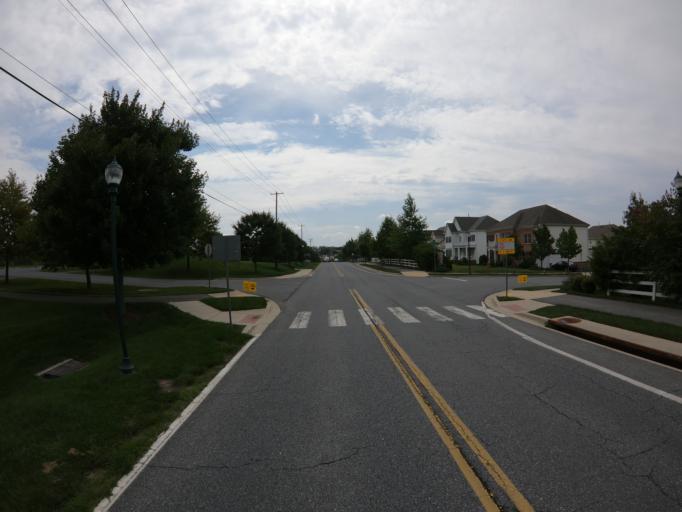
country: US
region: Maryland
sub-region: Montgomery County
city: Clarksburg
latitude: 39.2383
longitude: -77.2517
